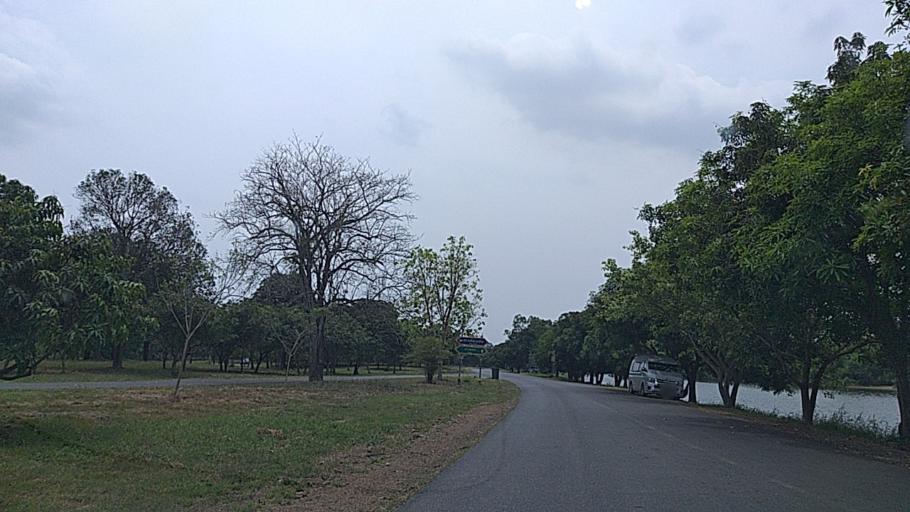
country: TH
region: Bangkok
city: Thawi Watthana
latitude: 13.7745
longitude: 100.3110
